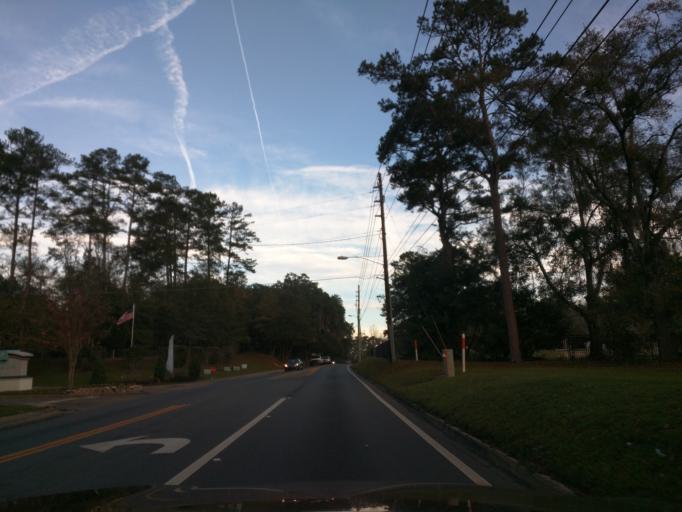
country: US
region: Florida
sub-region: Leon County
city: Tallahassee
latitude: 30.4596
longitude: -84.2965
